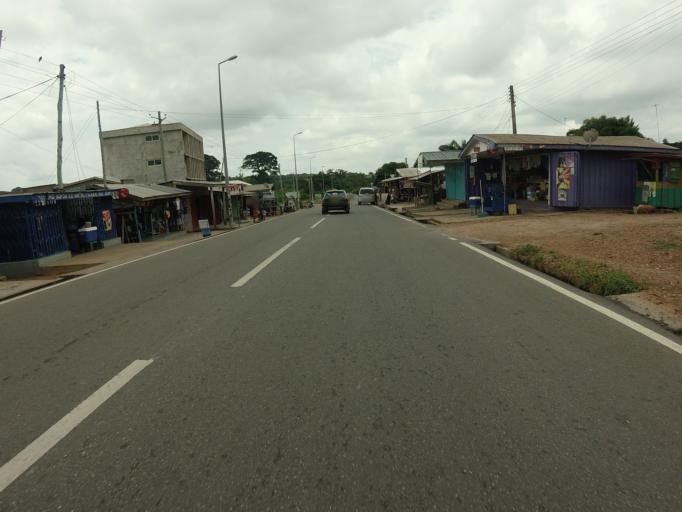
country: GH
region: Volta
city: Ho
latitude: 6.6091
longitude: 0.4804
